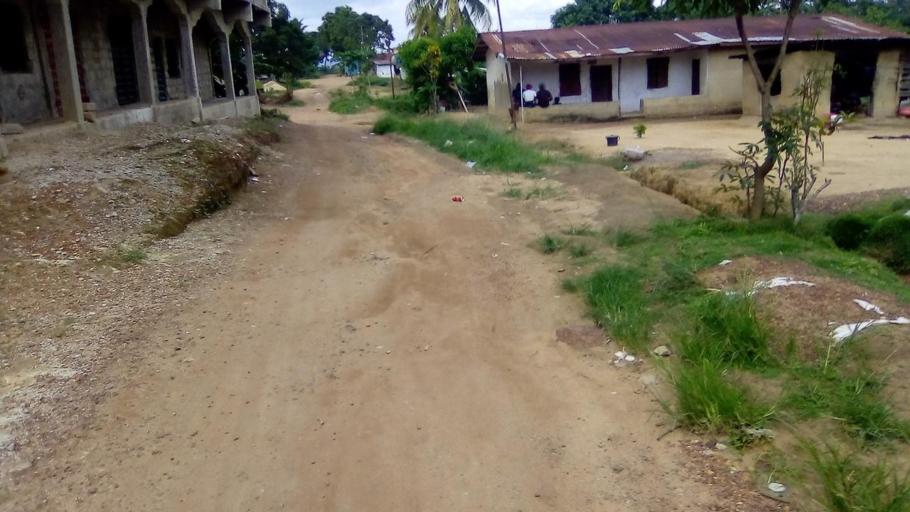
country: SL
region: Southern Province
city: Bo
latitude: 7.9587
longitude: -11.7205
